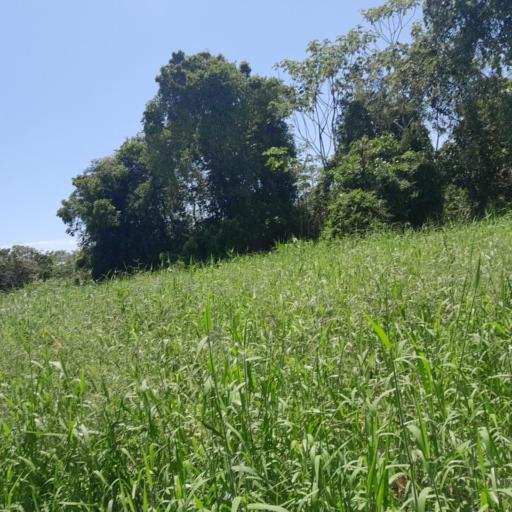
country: PE
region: Ucayali
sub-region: Provincia de Coronel Portillo
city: Puerto Callao
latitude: -8.2669
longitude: -74.6434
